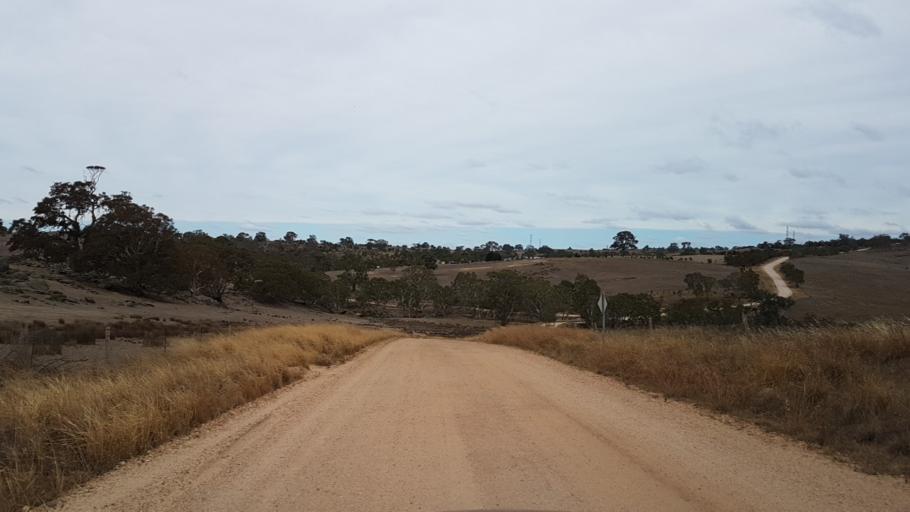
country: AU
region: South Australia
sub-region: Adelaide Hills
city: Birdwood
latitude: -34.8765
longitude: 139.0844
